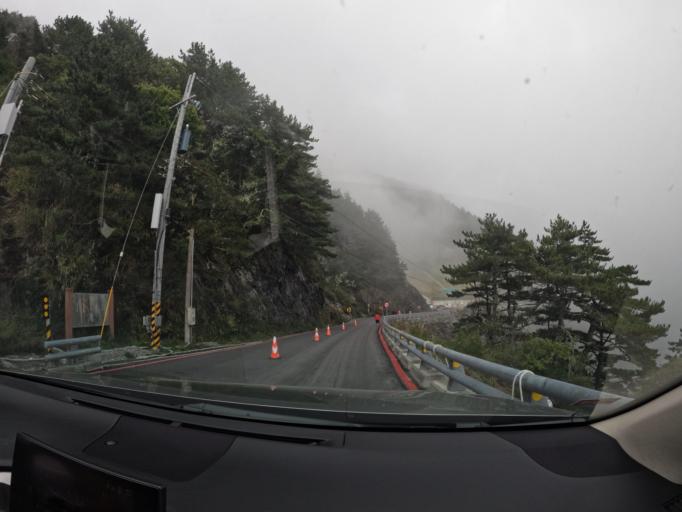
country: TW
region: Taiwan
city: Yujing
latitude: 23.2646
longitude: 120.9619
